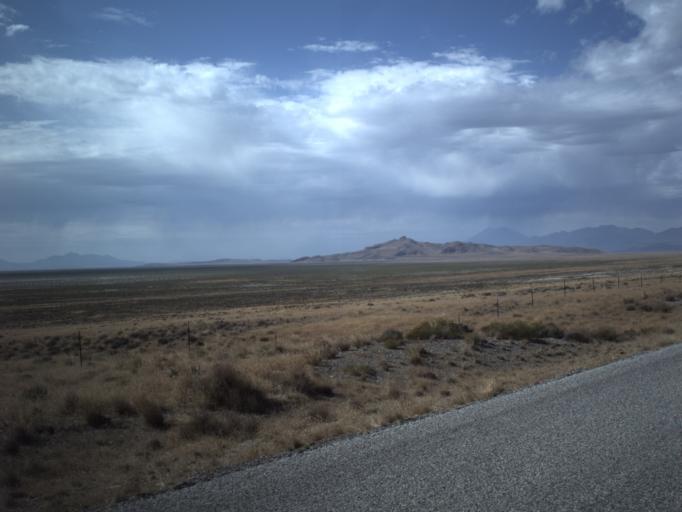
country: US
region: Utah
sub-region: Tooele County
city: Wendover
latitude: 41.4472
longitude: -113.6802
